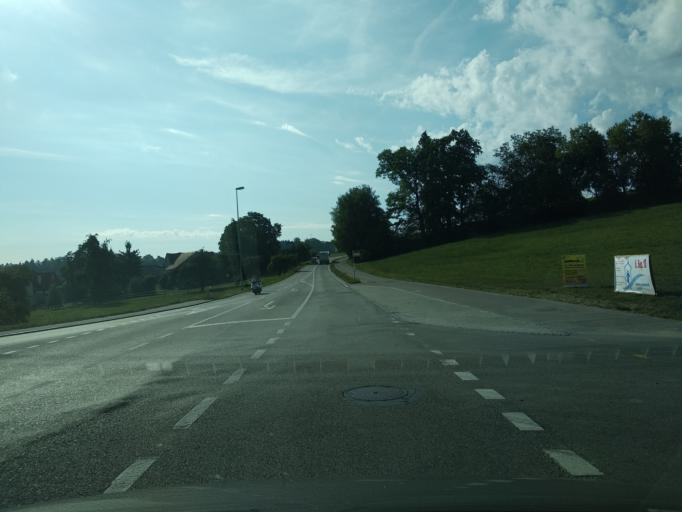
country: CH
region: Thurgau
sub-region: Frauenfeld District
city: Huttwilen
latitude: 47.5964
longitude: 8.8897
